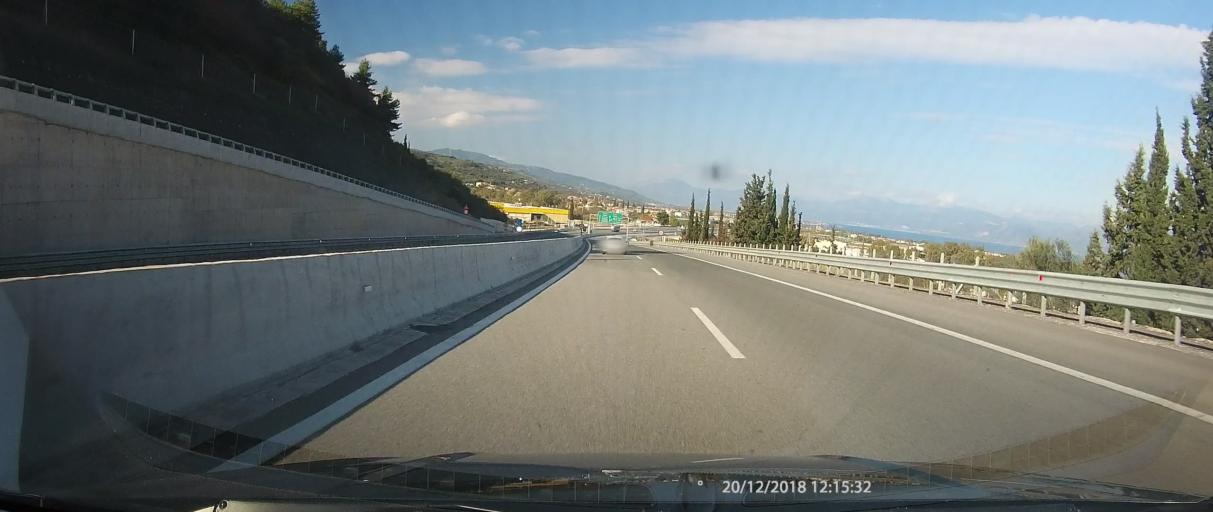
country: GR
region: West Greece
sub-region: Nomos Achaias
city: Aigio
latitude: 38.2556
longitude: 22.0664
